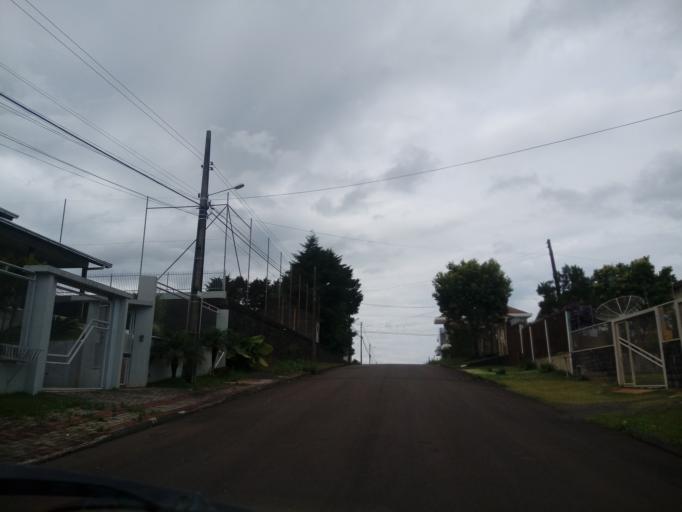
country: BR
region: Santa Catarina
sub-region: Chapeco
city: Chapeco
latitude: -27.0769
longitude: -52.6155
